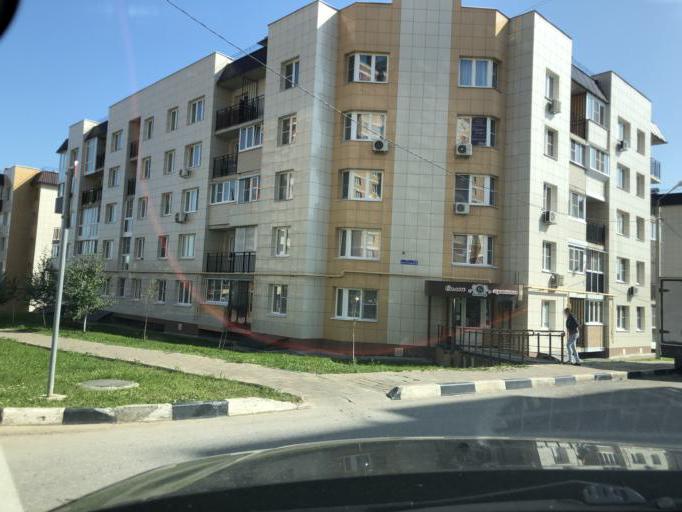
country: RU
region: Tula
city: Tula
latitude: 54.1749
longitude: 37.6542
